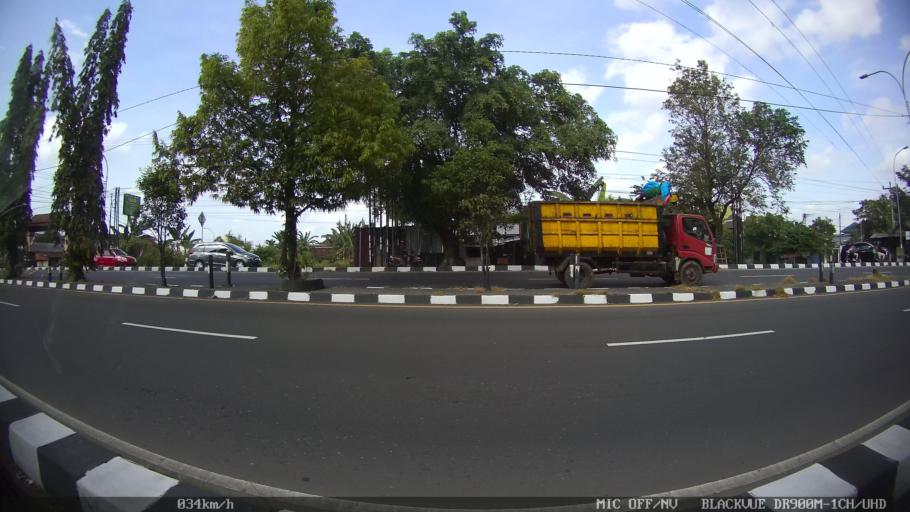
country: ID
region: Daerah Istimewa Yogyakarta
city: Kasihan
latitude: -7.8332
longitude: 110.3581
